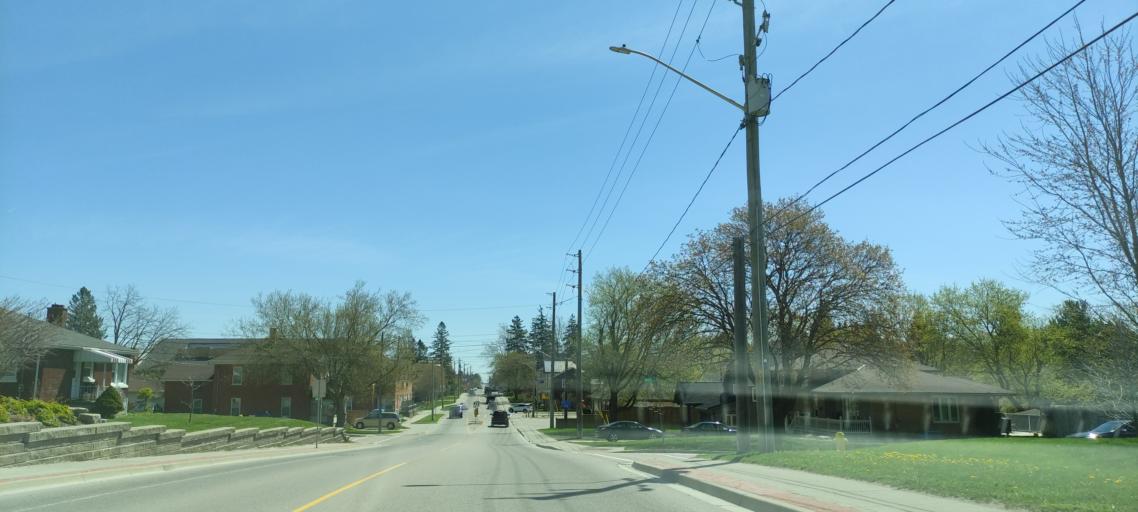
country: CA
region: Ontario
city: Waterloo
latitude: 43.6006
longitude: -80.5650
